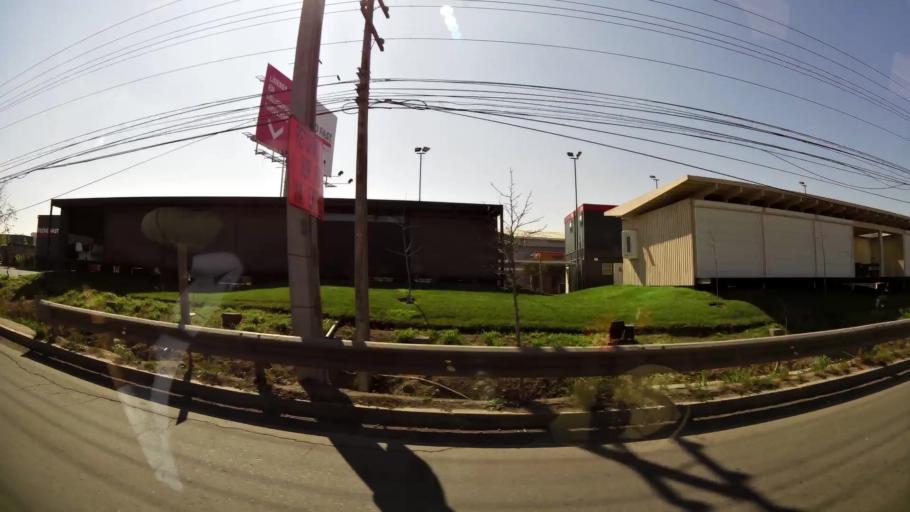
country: CL
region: Santiago Metropolitan
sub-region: Provincia de Chacabuco
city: Chicureo Abajo
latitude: -33.3091
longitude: -70.7254
